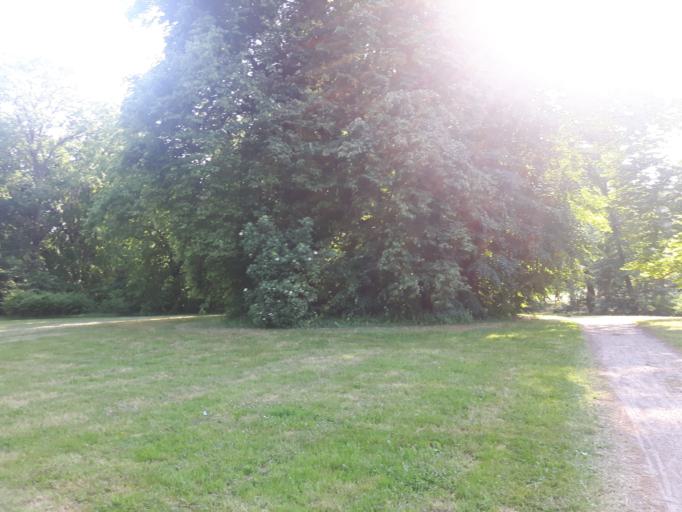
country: DE
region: Mecklenburg-Vorpommern
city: Putbus
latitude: 54.3471
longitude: 13.4690
